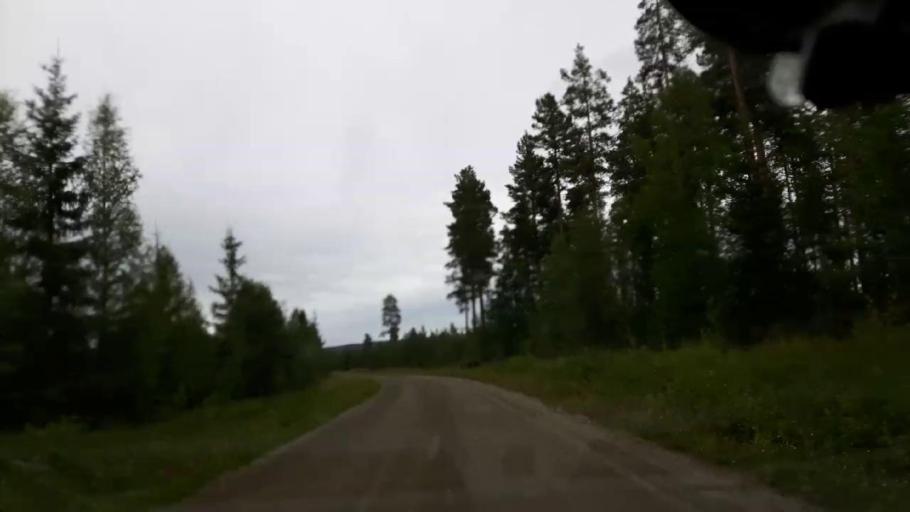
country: SE
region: Jaemtland
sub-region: Braecke Kommun
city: Braecke
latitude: 62.9405
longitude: 15.4534
